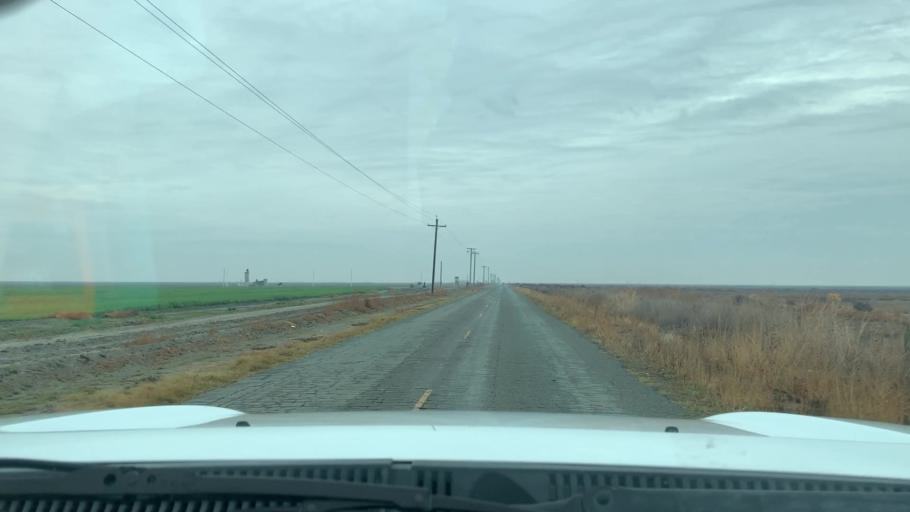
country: US
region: California
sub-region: Tulare County
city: Alpaugh
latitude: 35.7609
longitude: -119.5326
